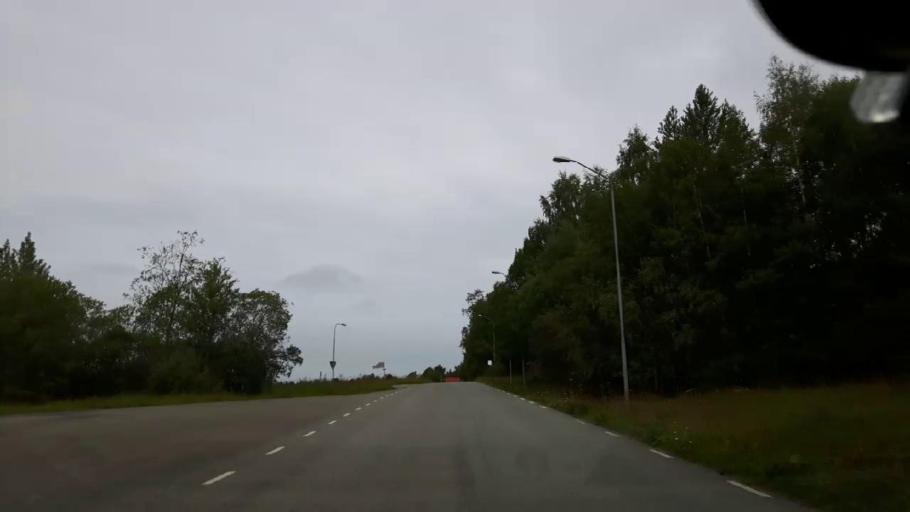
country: SE
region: Jaemtland
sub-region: OEstersunds Kommun
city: Ostersund
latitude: 63.1665
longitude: 14.5264
